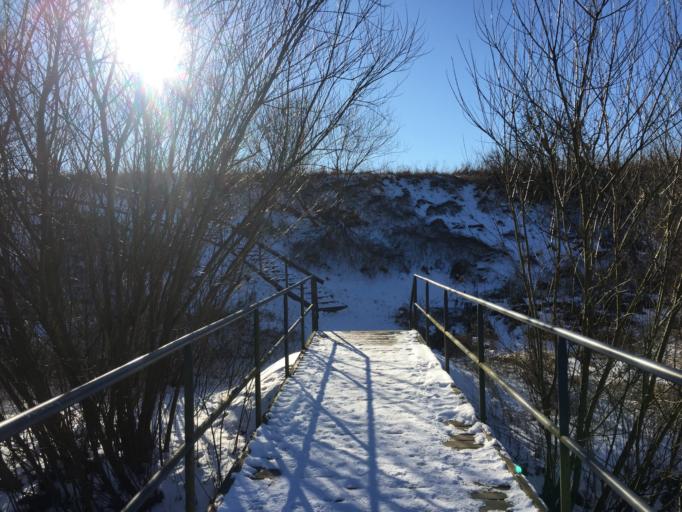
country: SE
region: Skane
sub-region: Staffanstorps Kommun
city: Hjaerup
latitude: 55.6981
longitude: 13.1552
